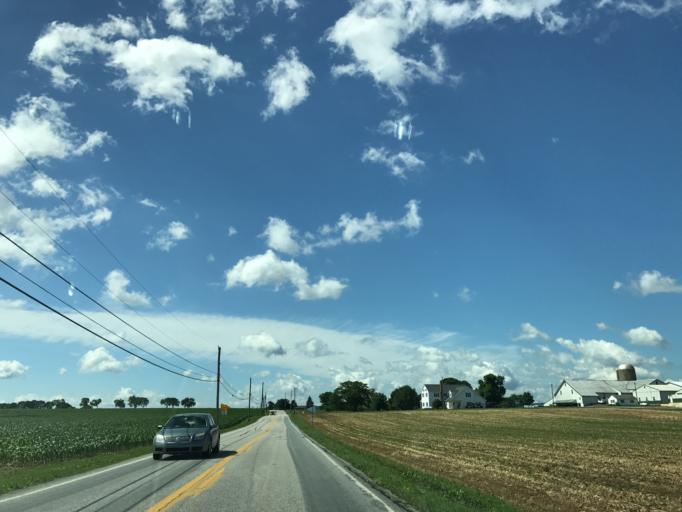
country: US
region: Pennsylvania
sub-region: Lancaster County
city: Maytown
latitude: 40.1042
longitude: -76.5913
